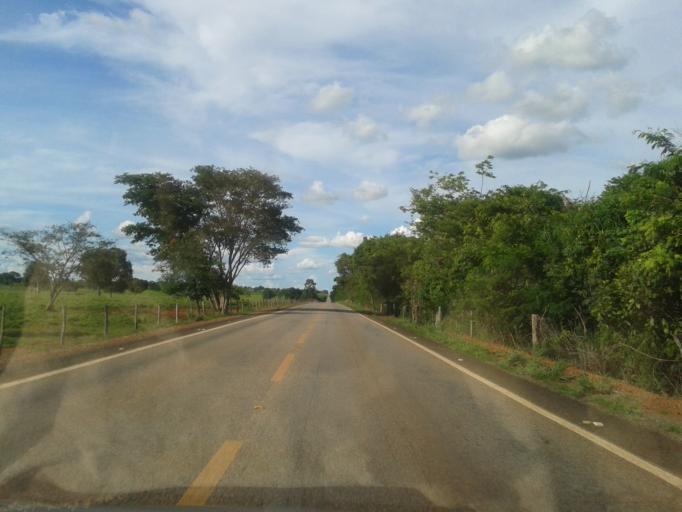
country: BR
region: Goias
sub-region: Mozarlandia
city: Mozarlandia
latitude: -14.2827
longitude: -50.4013
